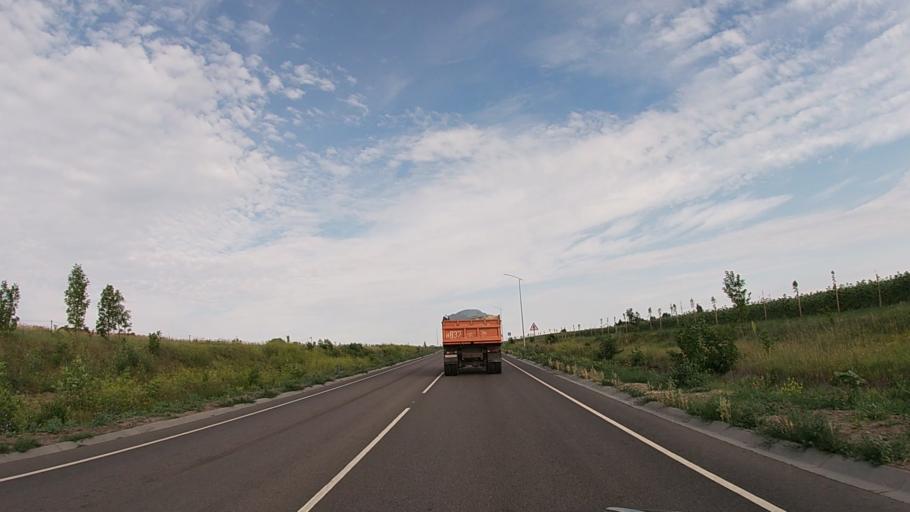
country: RU
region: Belgorod
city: Severnyy
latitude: 50.6708
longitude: 36.4838
